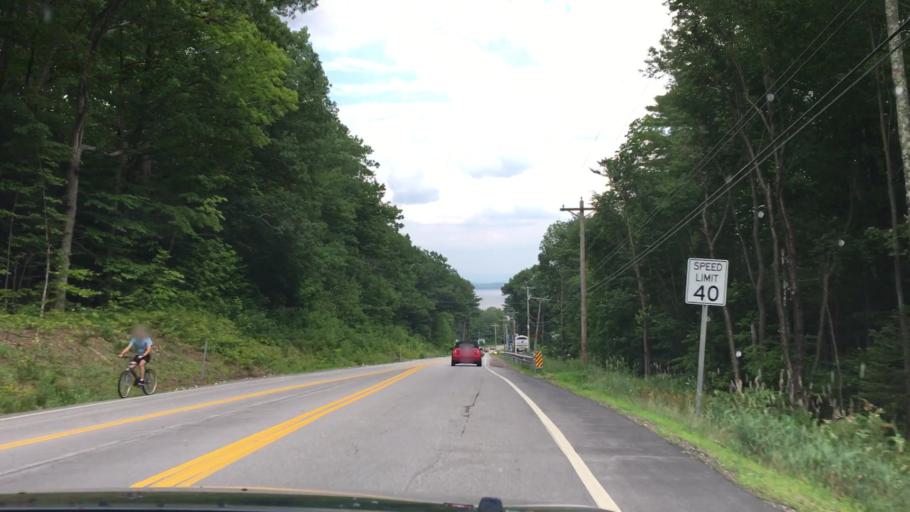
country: US
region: New Hampshire
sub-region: Belknap County
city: Meredith
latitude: 43.6381
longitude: -71.4962
